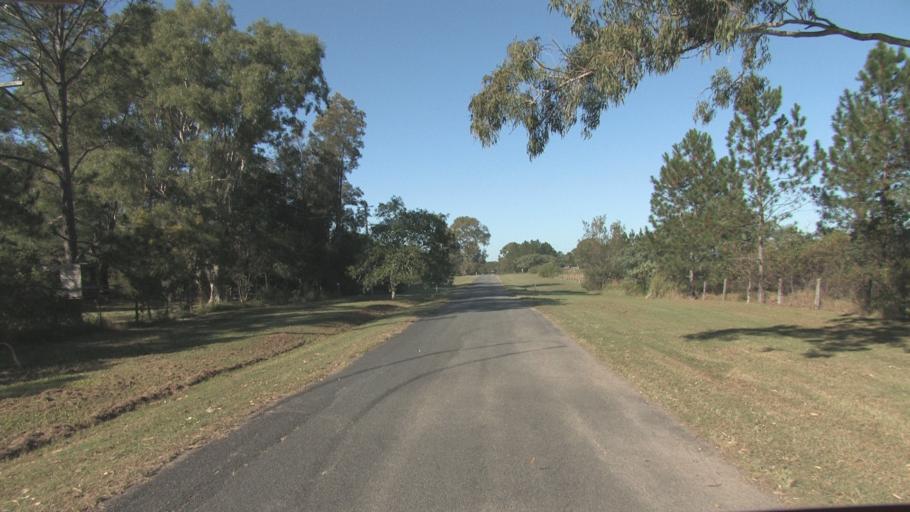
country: AU
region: Queensland
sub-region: Gold Coast
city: Yatala
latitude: -27.6875
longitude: 153.2603
